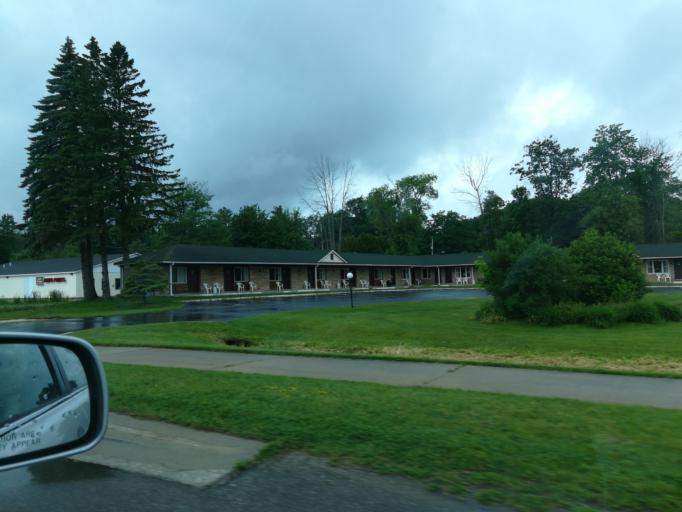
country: US
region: Michigan
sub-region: Iosco County
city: Tawas City
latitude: 44.2563
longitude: -83.5316
